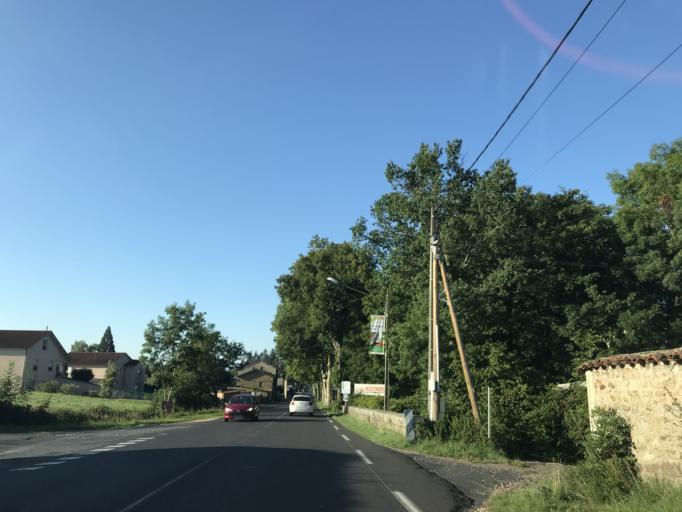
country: FR
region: Auvergne
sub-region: Departement du Puy-de-Dome
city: Ambert
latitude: 45.5623
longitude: 3.7430
